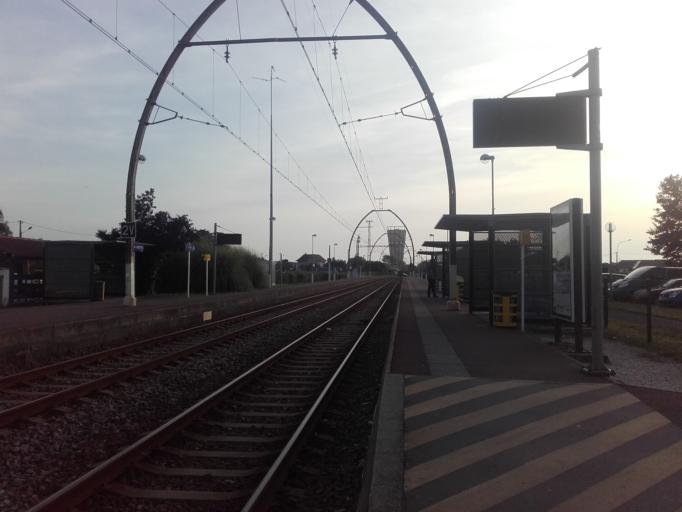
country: FR
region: Aquitaine
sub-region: Departement de la Gironde
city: Gujan-Mestras
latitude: 44.6406
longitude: -1.0691
